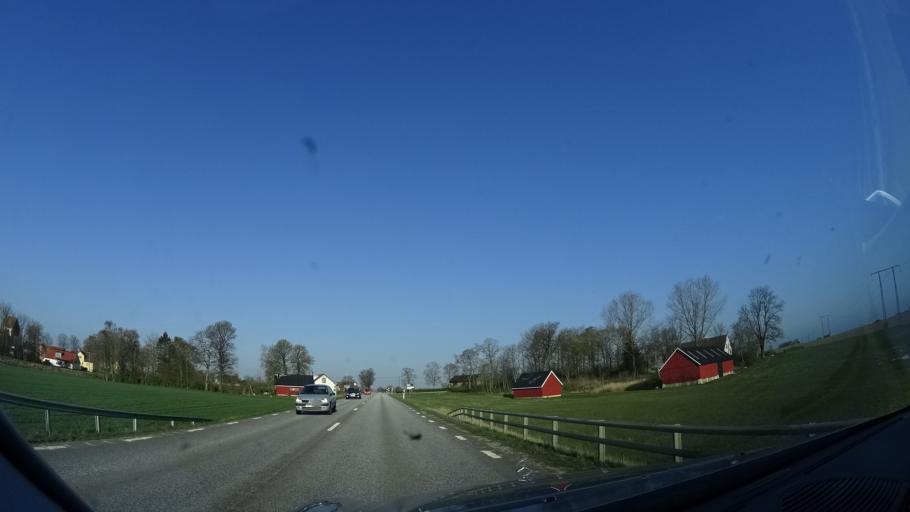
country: SE
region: Skane
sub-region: Svalovs Kommun
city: Teckomatorp
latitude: 55.8712
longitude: 13.1205
